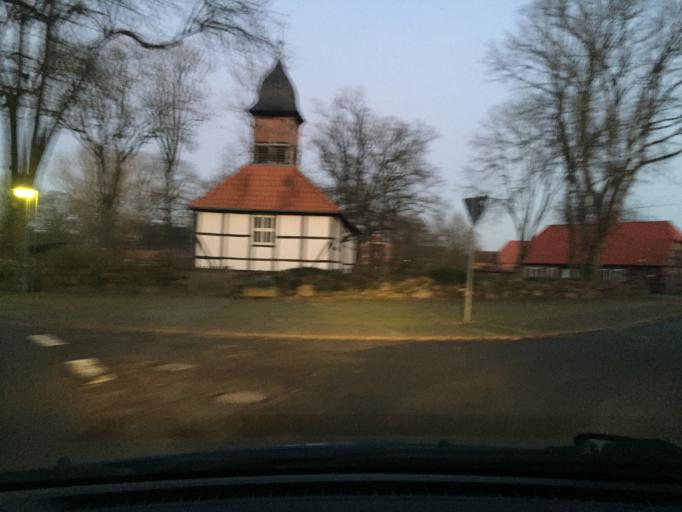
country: DE
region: Lower Saxony
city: Gohrde
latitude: 53.1846
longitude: 10.9301
